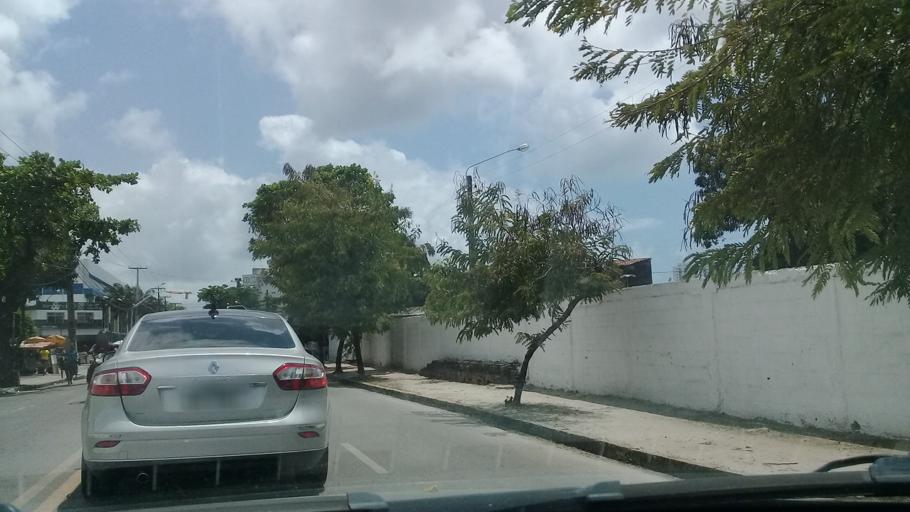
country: BR
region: Pernambuco
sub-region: Recife
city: Recife
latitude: -8.1084
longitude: -34.9166
